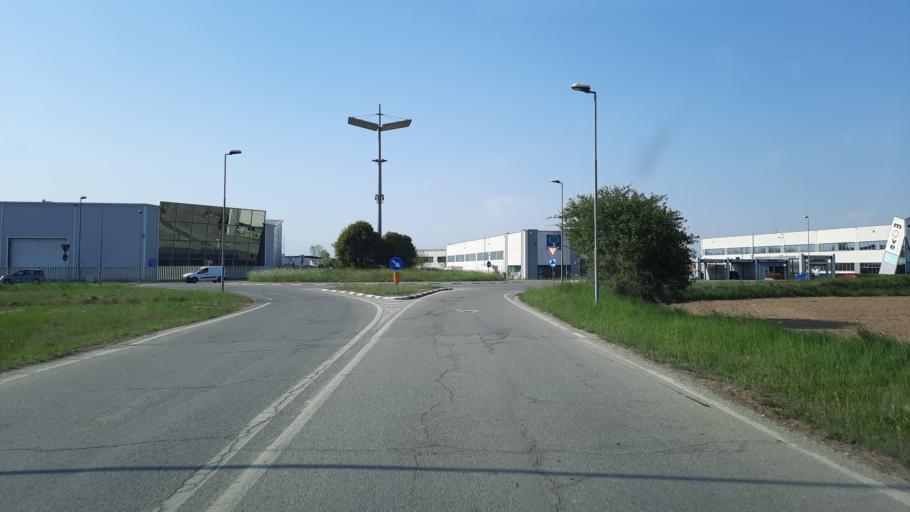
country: IT
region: Piedmont
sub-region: Provincia di Vercelli
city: Crescentino
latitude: 45.2003
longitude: 8.1103
